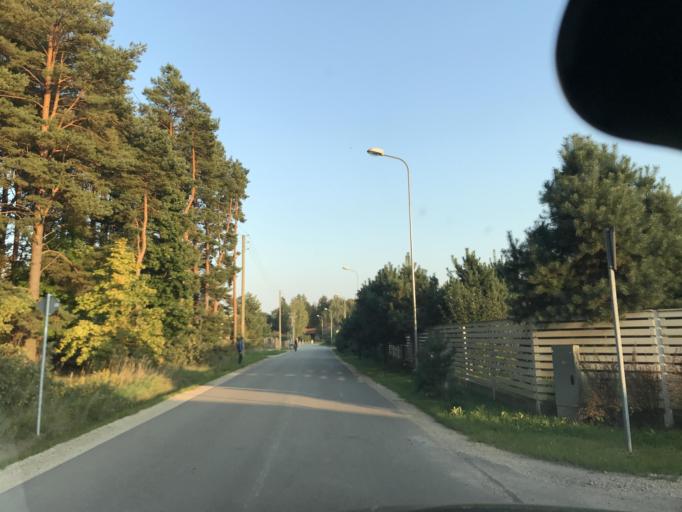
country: LV
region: Ikskile
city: Ikskile
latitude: 56.8245
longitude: 24.5103
